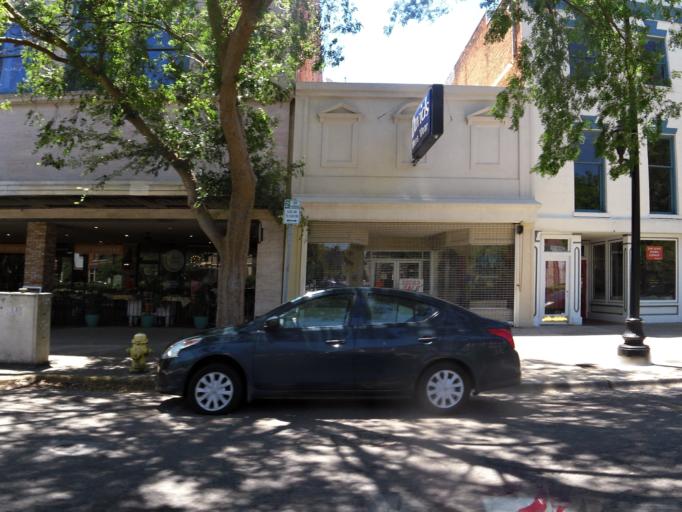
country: US
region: Georgia
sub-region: Richmond County
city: Augusta
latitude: 33.4763
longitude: -81.9688
